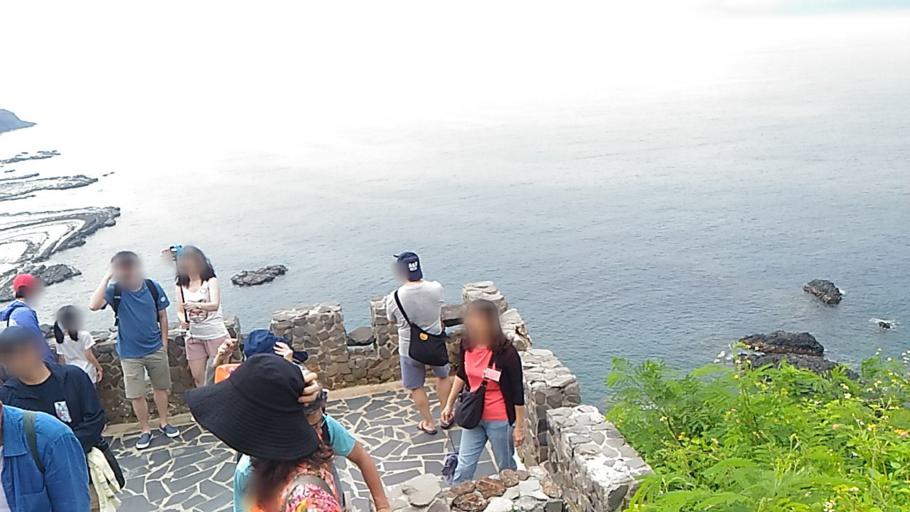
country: TW
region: Taiwan
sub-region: Penghu
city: Ma-kung
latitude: 23.2018
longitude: 119.4353
